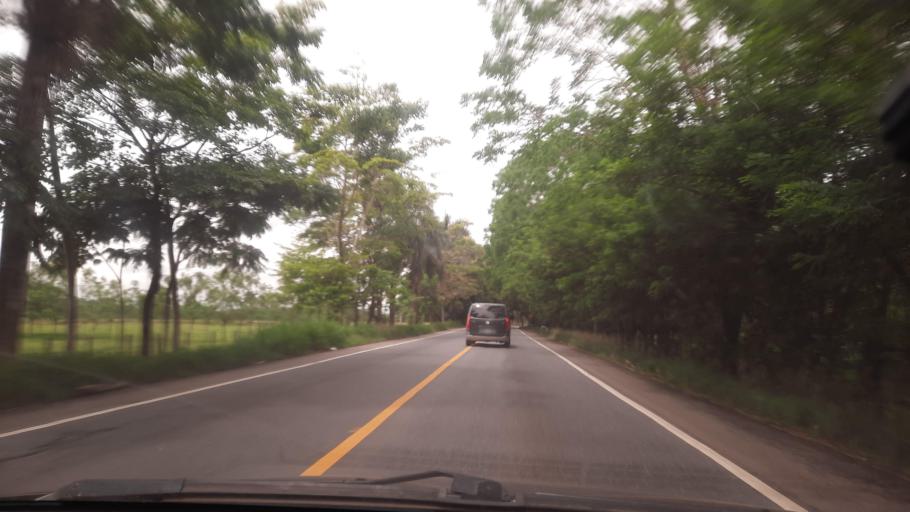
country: GT
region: Izabal
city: Morales
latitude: 15.4667
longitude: -88.9087
